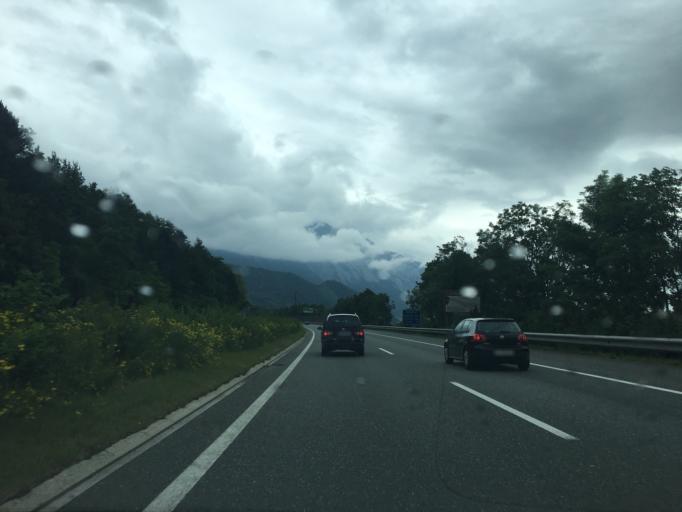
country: AT
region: Tyrol
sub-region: Politischer Bezirk Schwaz
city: Vomp
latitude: 47.3353
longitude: 11.6834
